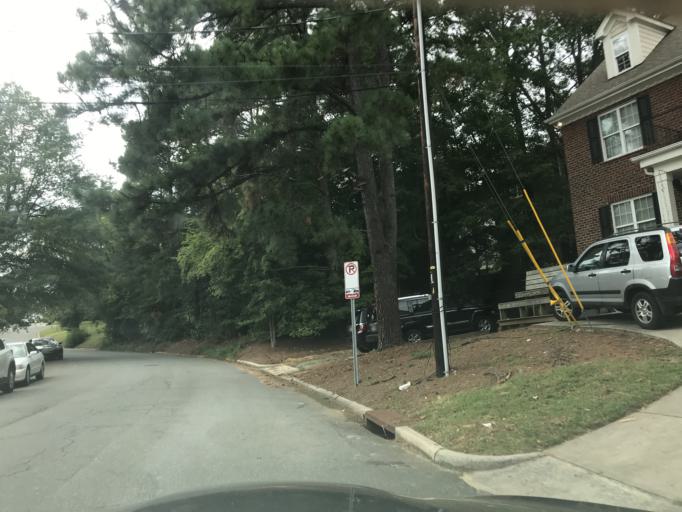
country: US
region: North Carolina
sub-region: Orange County
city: Chapel Hill
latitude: 35.9202
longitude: -79.0585
